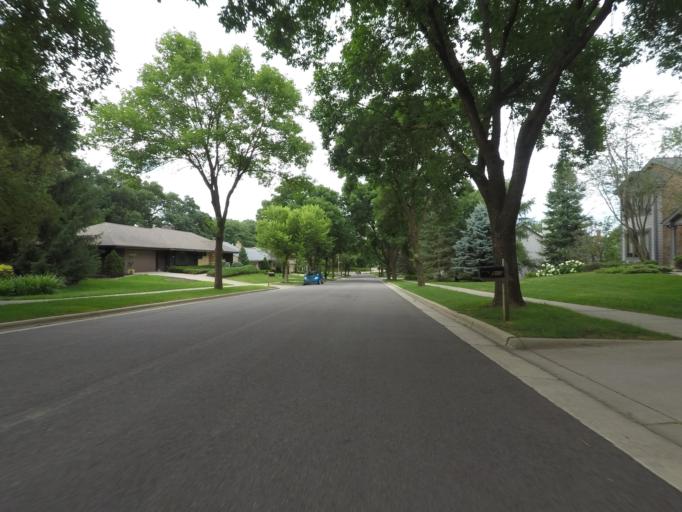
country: US
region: Wisconsin
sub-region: Dane County
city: Middleton
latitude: 43.0803
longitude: -89.4966
